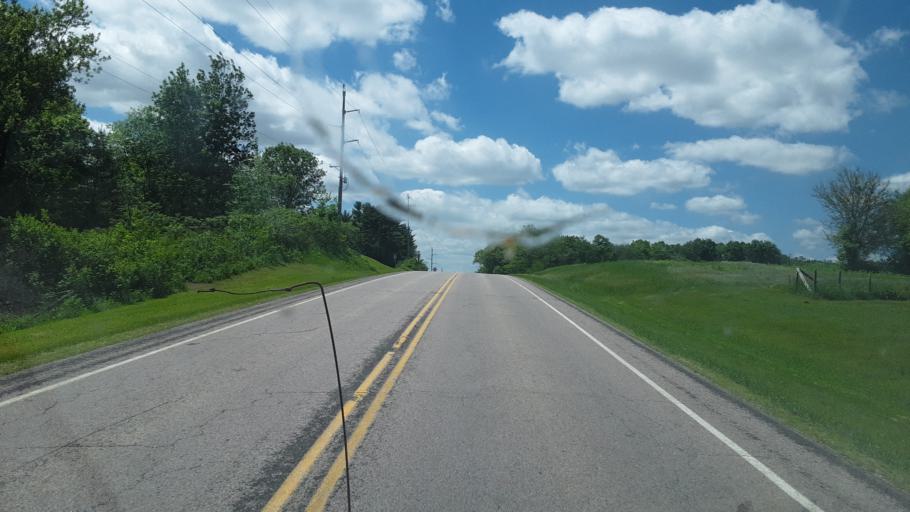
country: US
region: Wisconsin
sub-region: Sauk County
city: Lake Delton
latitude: 43.5910
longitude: -89.8716
